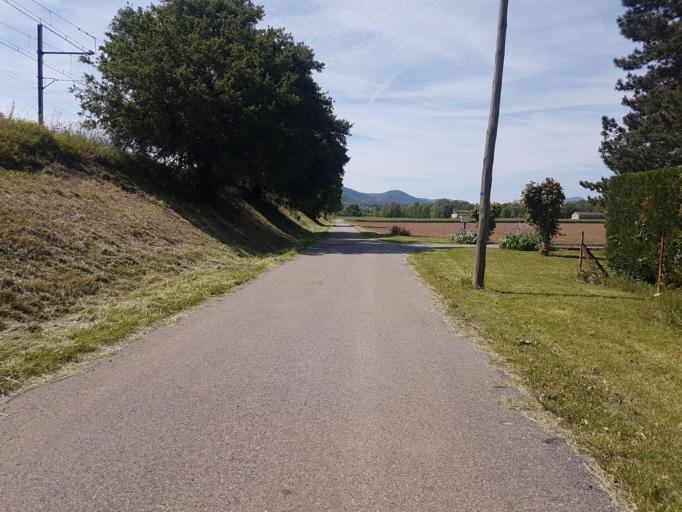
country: FR
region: Rhone-Alpes
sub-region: Departement de l'Ardeche
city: Le Pouzin
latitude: 44.7365
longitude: 4.7474
